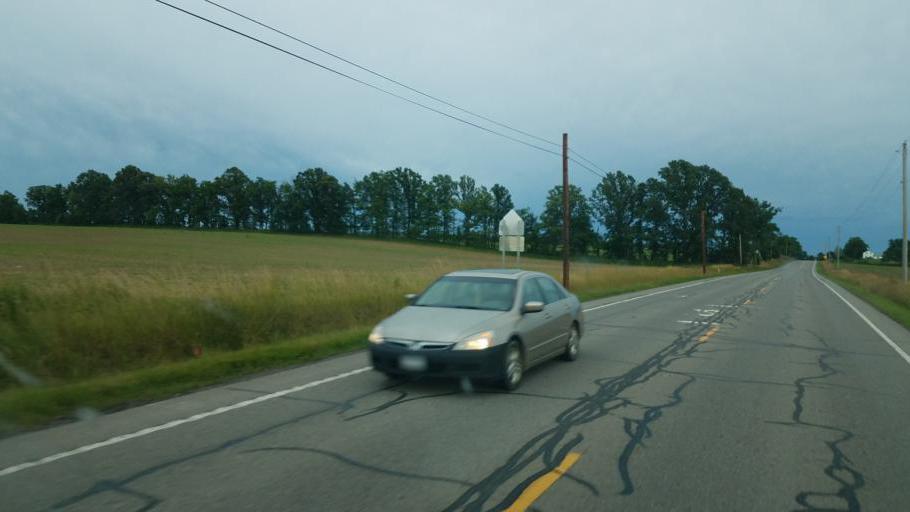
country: US
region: Ohio
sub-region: Huron County
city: Greenwich
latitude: 40.9439
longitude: -82.4948
